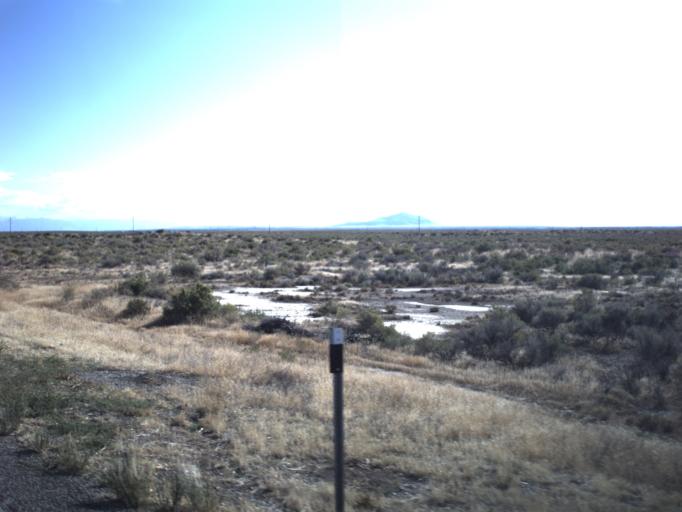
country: US
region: Utah
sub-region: Millard County
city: Delta
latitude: 39.3045
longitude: -112.4738
